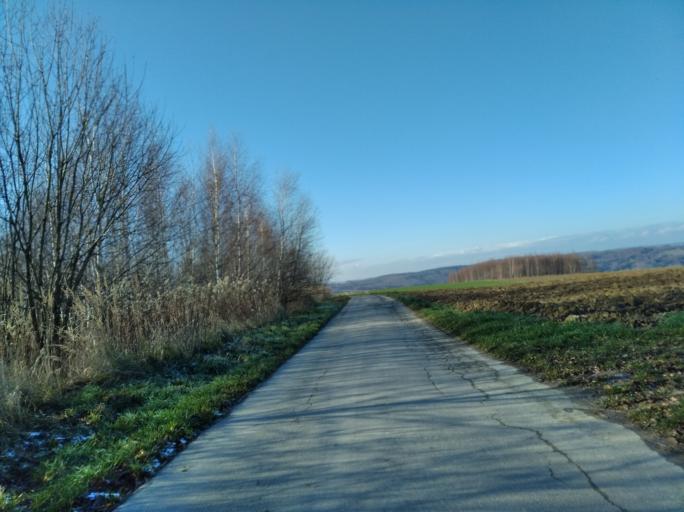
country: PL
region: Subcarpathian Voivodeship
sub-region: Powiat strzyzowski
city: Strzyzow
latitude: 49.8837
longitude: 21.8433
